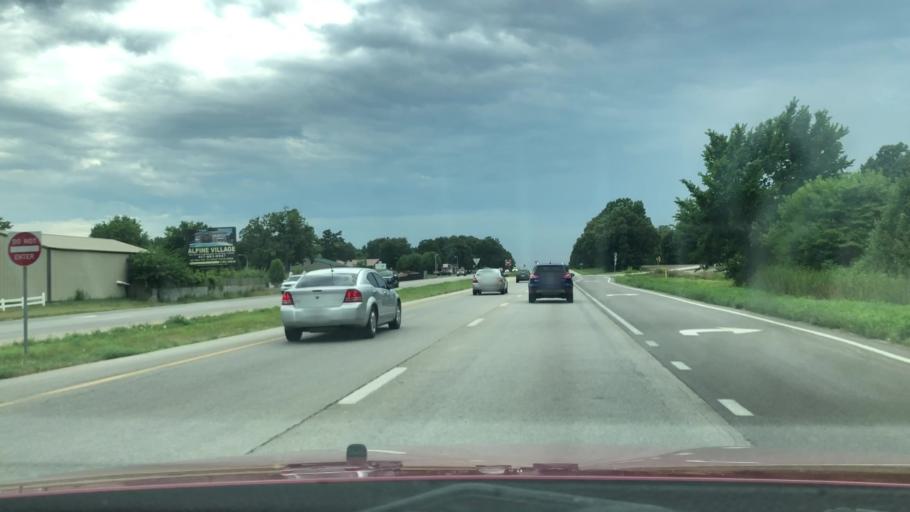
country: US
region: Missouri
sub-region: Greene County
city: Republic
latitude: 37.1403
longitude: -93.4413
